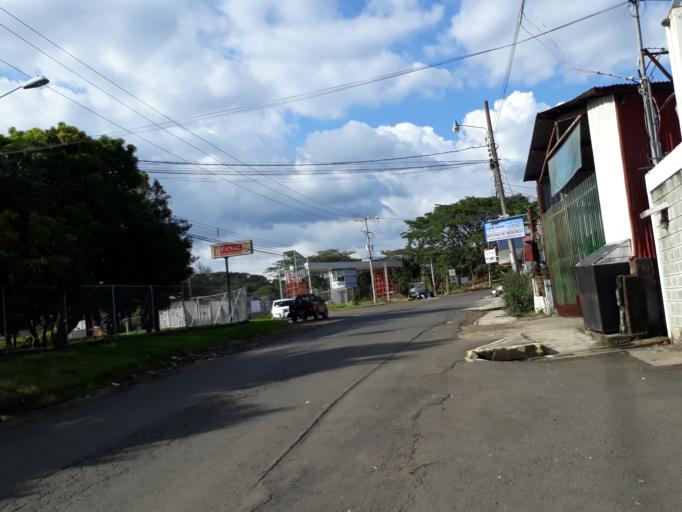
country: CR
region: Alajuela
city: Atenas
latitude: 10.0181
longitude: -84.3417
